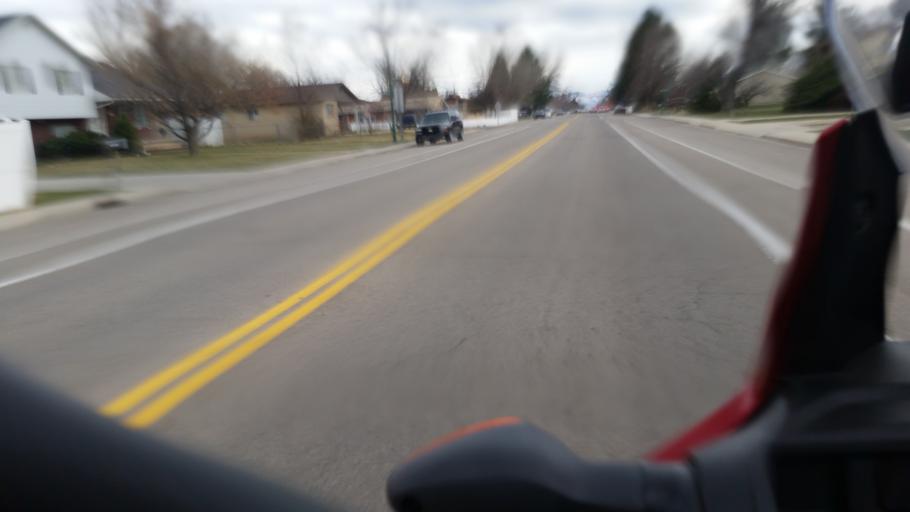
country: US
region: Utah
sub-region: Utah County
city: Orem
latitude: 40.3144
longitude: -111.6863
